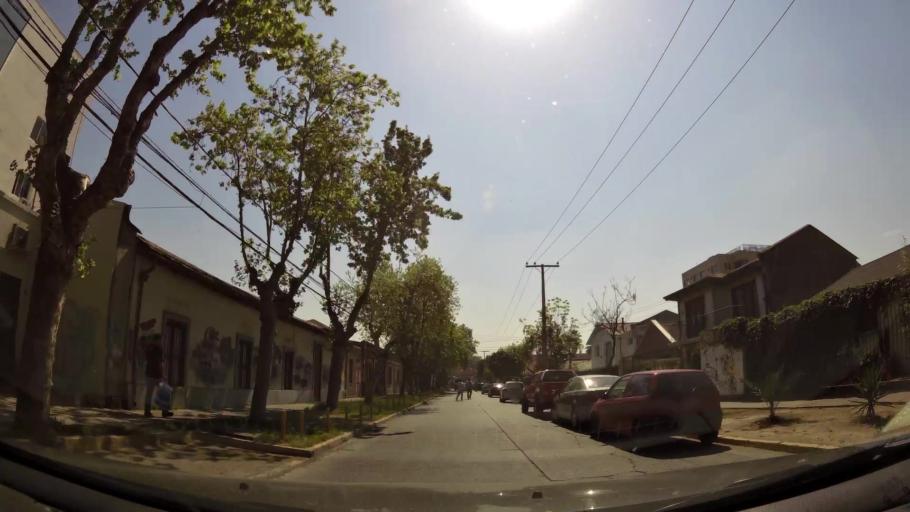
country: CL
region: Santiago Metropolitan
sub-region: Provincia de Maipo
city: San Bernardo
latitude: -33.5908
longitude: -70.7076
